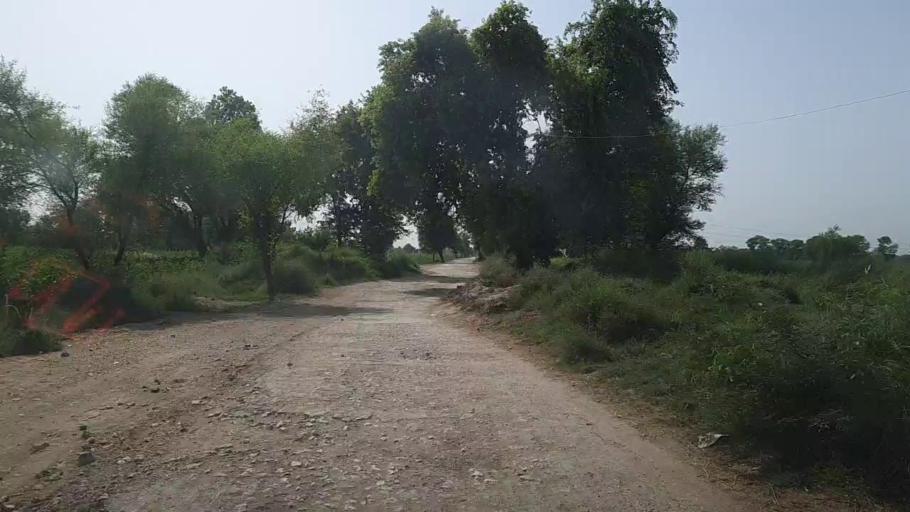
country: PK
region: Sindh
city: Pad Idan
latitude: 26.7674
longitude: 68.3202
